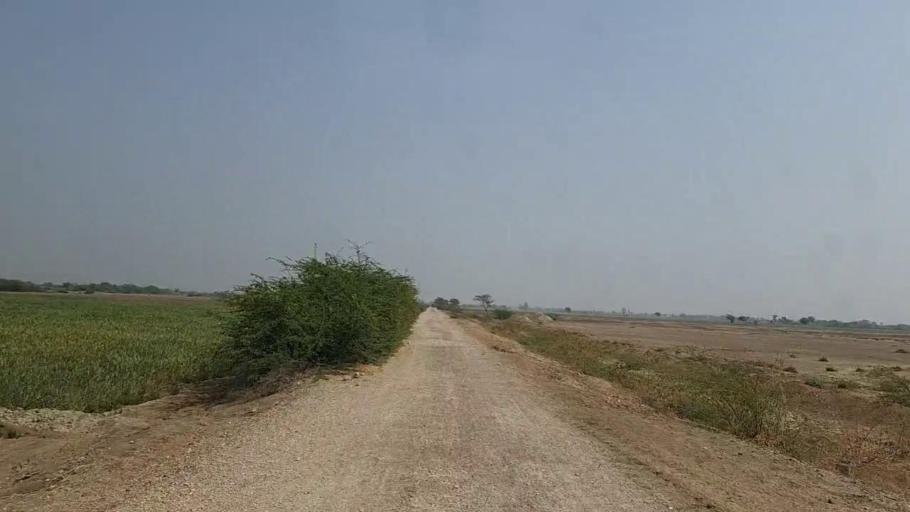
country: PK
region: Sindh
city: Naukot
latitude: 24.8097
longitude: 69.3640
